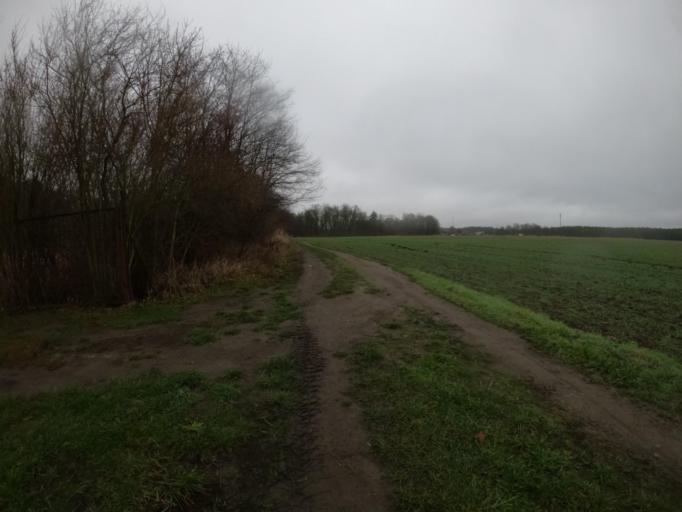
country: PL
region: West Pomeranian Voivodeship
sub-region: Powiat mysliborski
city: Debno
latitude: 52.7803
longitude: 14.7626
